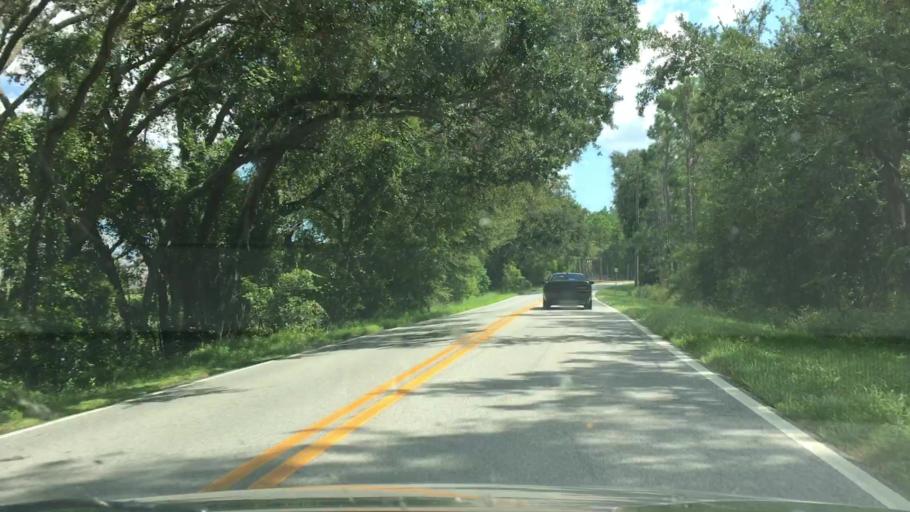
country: US
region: Florida
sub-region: Lake County
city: Minneola
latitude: 28.5687
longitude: -81.7100
